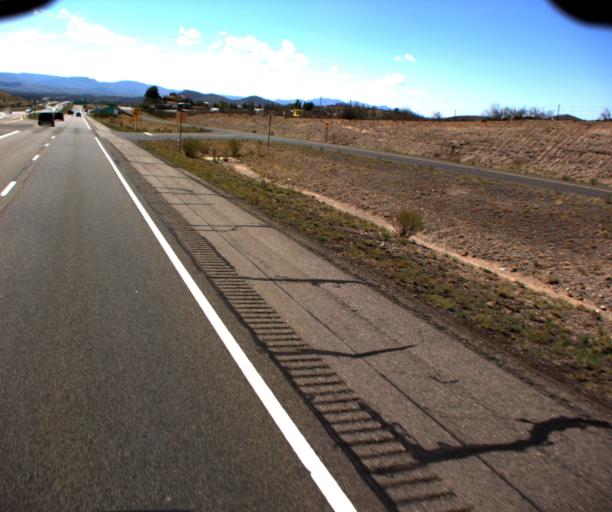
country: US
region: Arizona
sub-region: Yavapai County
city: Spring Valley
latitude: 34.3393
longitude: -112.1345
